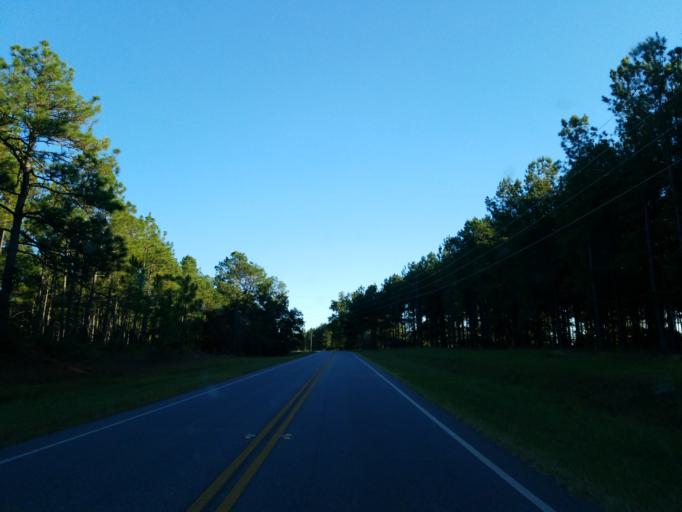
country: US
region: Georgia
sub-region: Worth County
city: Sylvester
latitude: 31.5912
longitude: -83.8635
